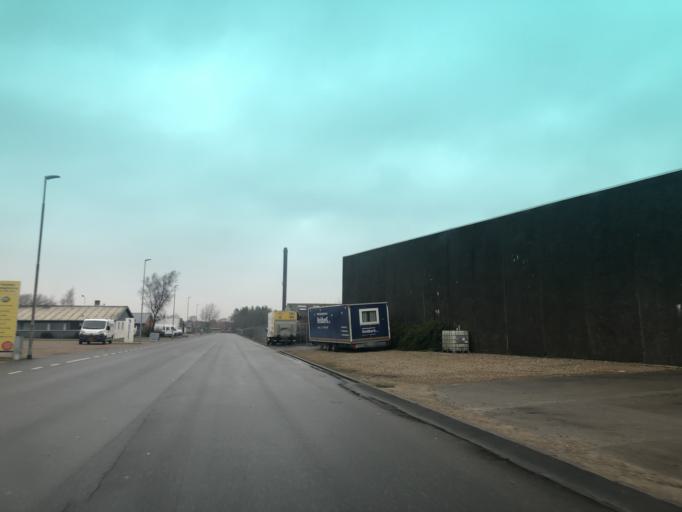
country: DK
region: Central Jutland
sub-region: Struer Kommune
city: Struer
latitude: 56.4859
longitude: 8.5787
